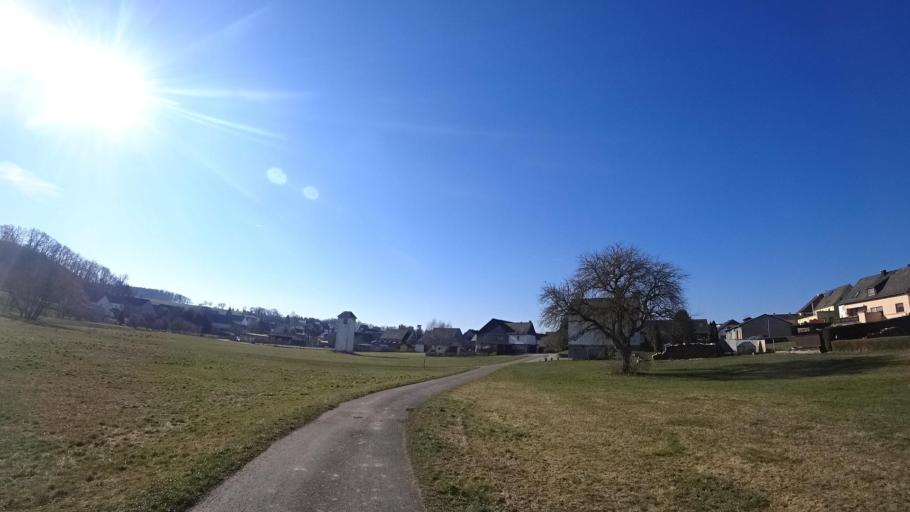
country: DE
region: Rheinland-Pfalz
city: Ohlweiler
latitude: 49.9680
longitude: 7.4977
